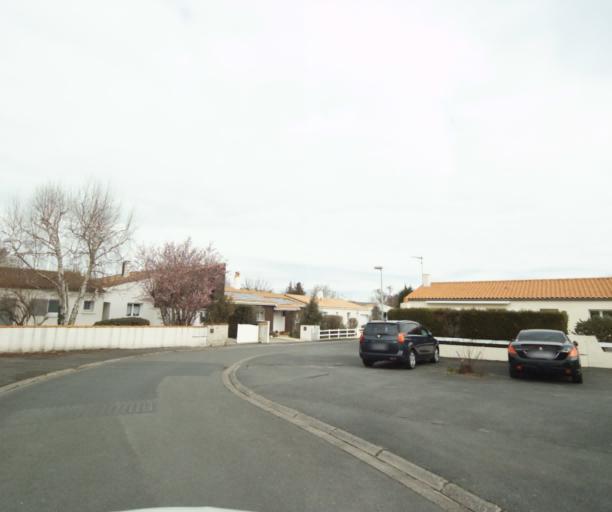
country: FR
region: Poitou-Charentes
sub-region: Departement de la Charente-Maritime
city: Lagord
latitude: 46.1901
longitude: -1.1501
